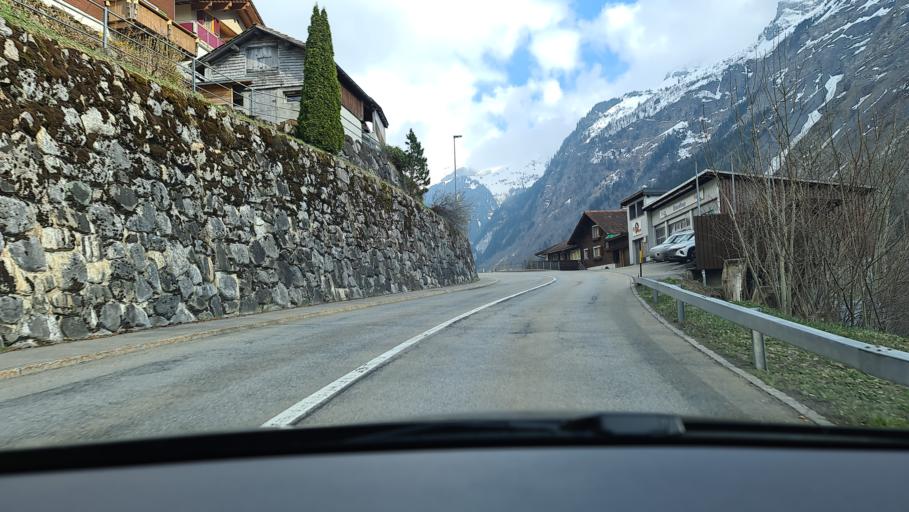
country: CH
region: Uri
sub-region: Uri
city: Burglen
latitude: 46.8723
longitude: 8.7324
